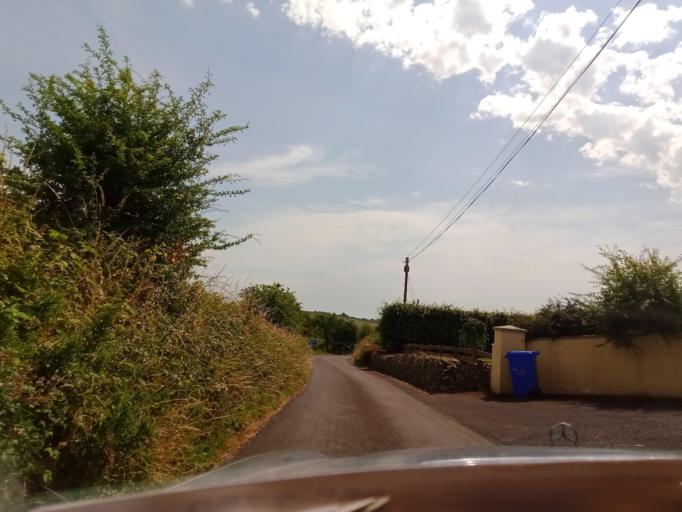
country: IE
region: Leinster
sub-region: Kilkenny
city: Mooncoin
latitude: 52.2702
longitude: -7.2137
